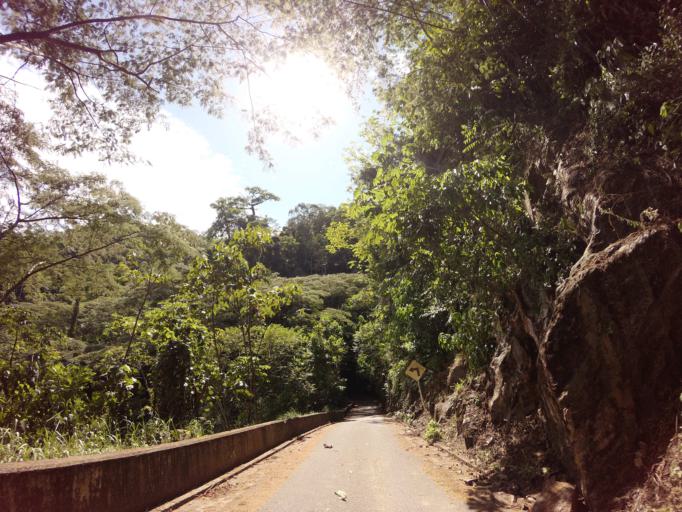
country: CO
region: Caldas
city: Norcasia
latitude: 5.5666
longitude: -74.9064
